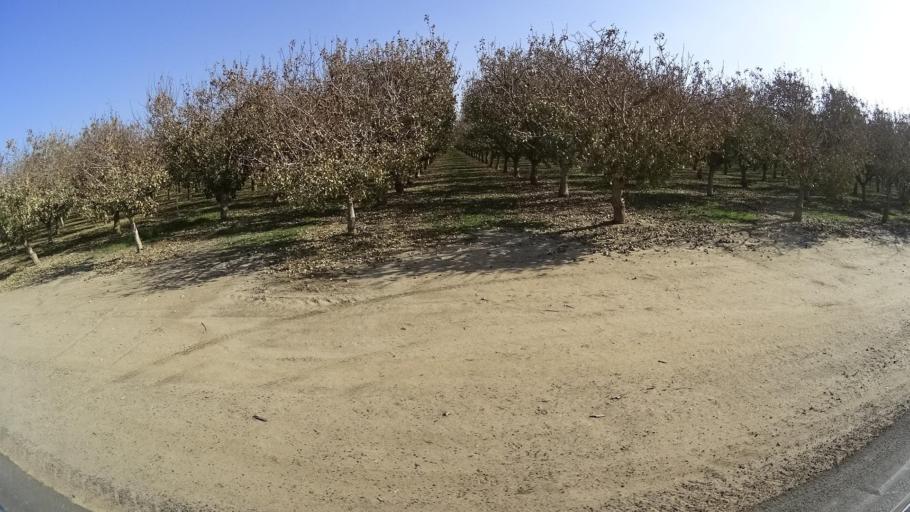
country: US
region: California
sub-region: Kern County
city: McFarland
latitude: 35.6417
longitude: -119.1867
